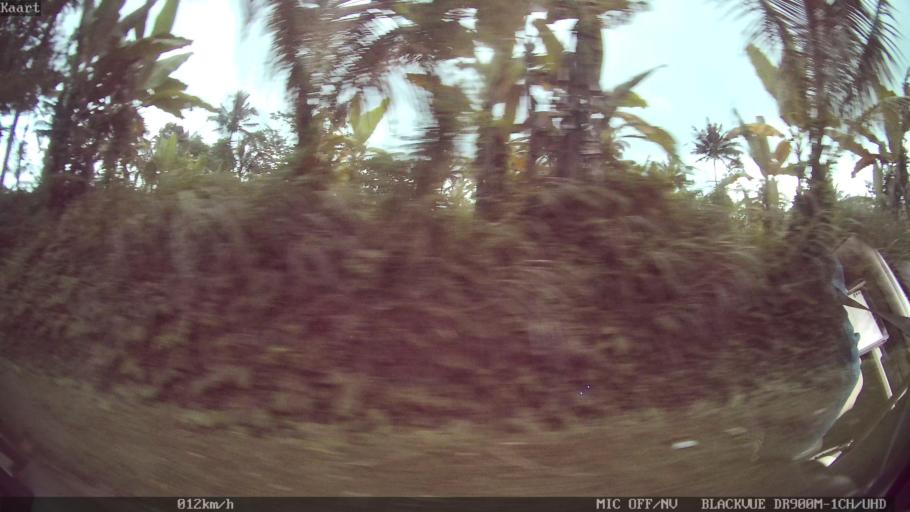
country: ID
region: Bali
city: Banjar Wangsian
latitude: -8.4412
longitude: 115.4259
